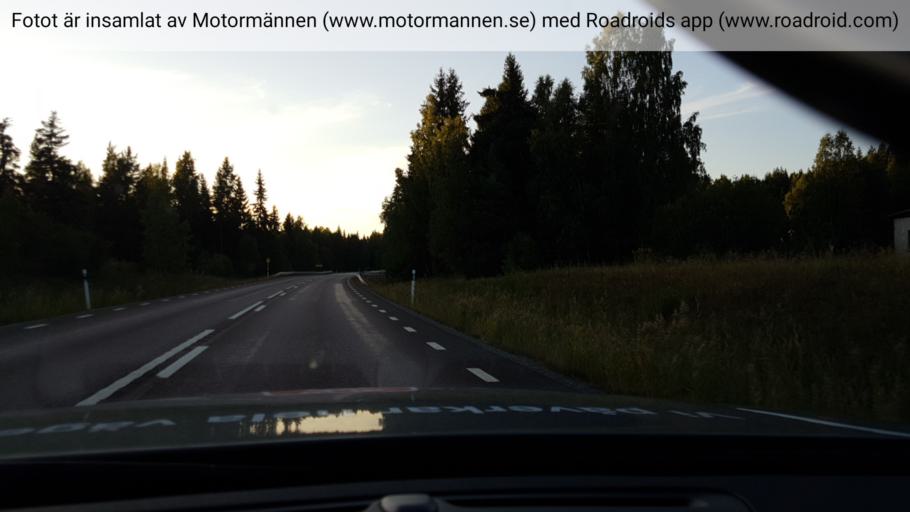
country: SE
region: Vaermland
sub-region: Storfors Kommun
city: Storfors
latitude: 59.4707
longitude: 14.3315
